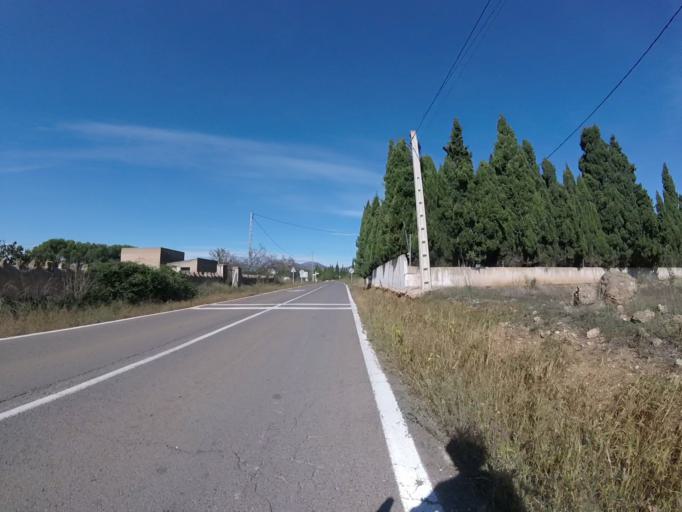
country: ES
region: Valencia
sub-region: Provincia de Castello
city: Benlloch
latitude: 40.2128
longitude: 0.0223
